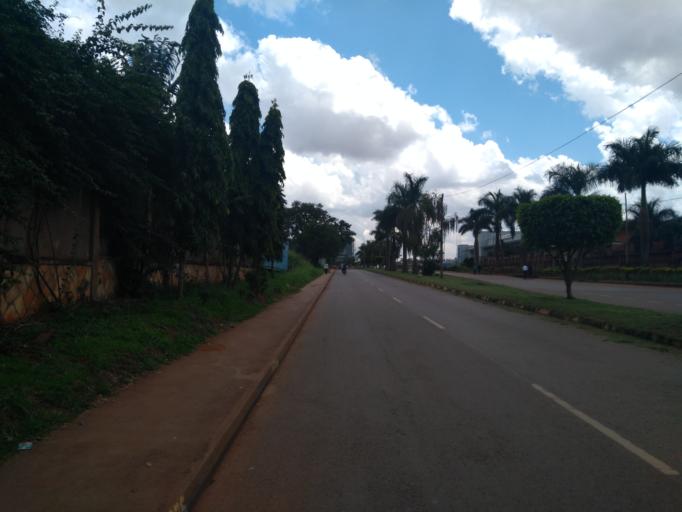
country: UG
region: Central Region
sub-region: Kampala District
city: Kampala
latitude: 0.3354
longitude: 32.6012
